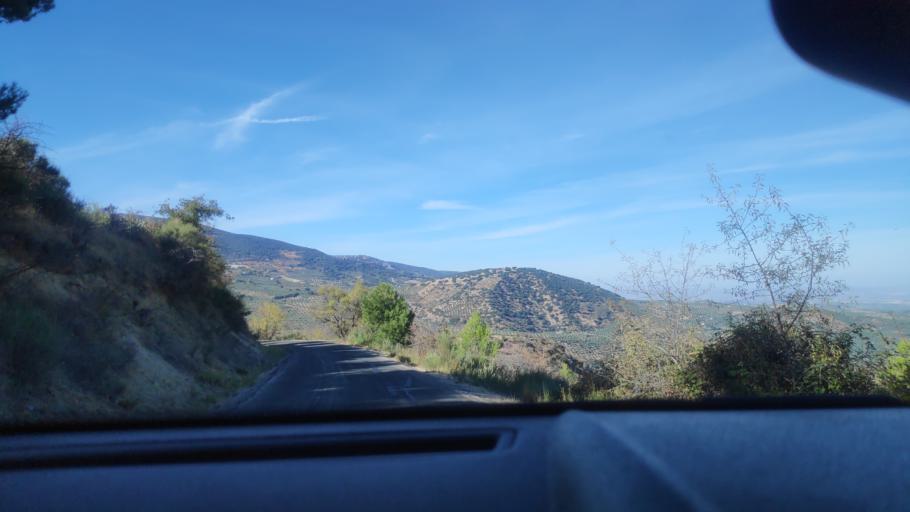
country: ES
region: Andalusia
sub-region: Provincia de Jaen
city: Torres
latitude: 37.7811
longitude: -3.4963
